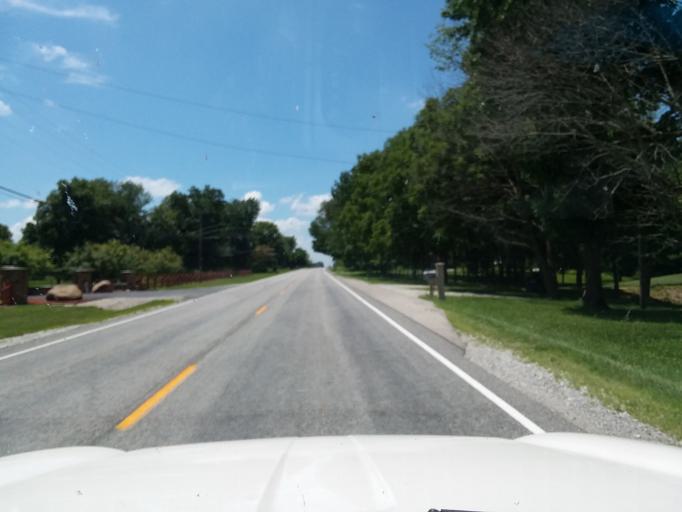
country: US
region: Indiana
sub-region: Johnson County
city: Trafalgar
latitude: 39.4094
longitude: -86.1019
